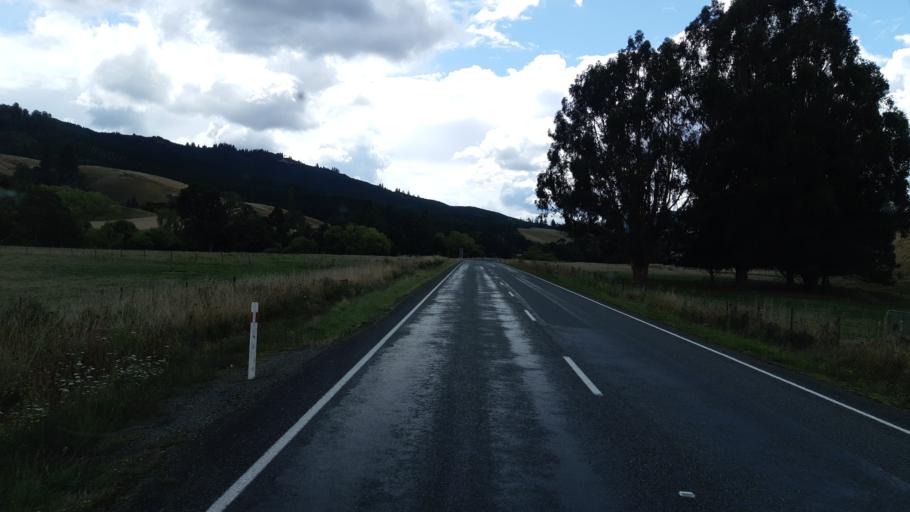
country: NZ
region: Tasman
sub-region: Tasman District
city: Wakefield
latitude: -41.5653
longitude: 172.7780
